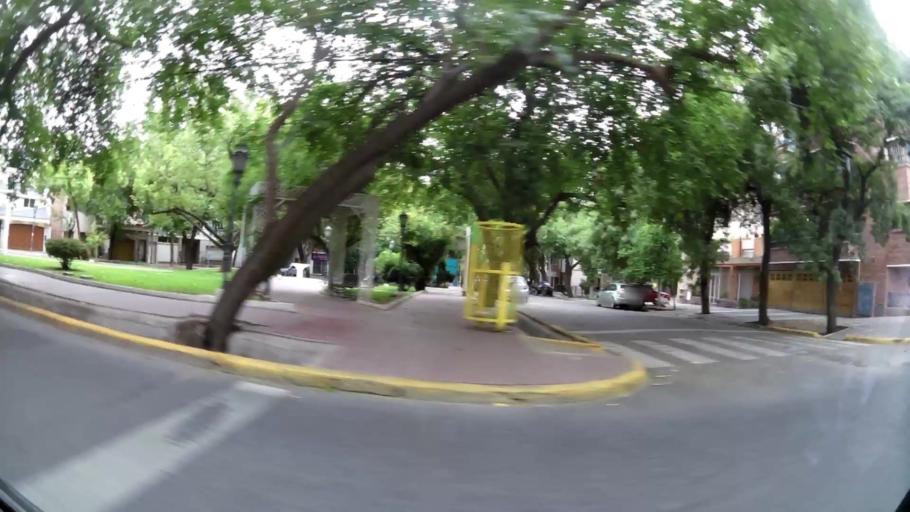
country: AR
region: Mendoza
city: Mendoza
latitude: -32.8855
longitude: -68.8512
